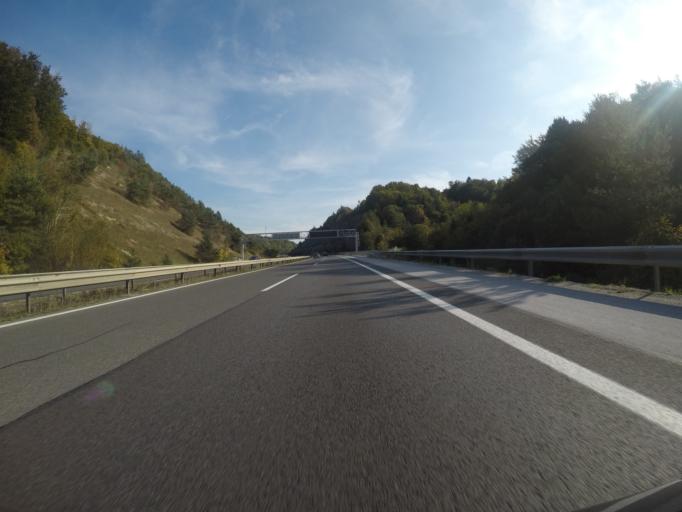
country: SI
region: Skofljica
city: Skofljica
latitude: 45.9990
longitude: 14.5843
